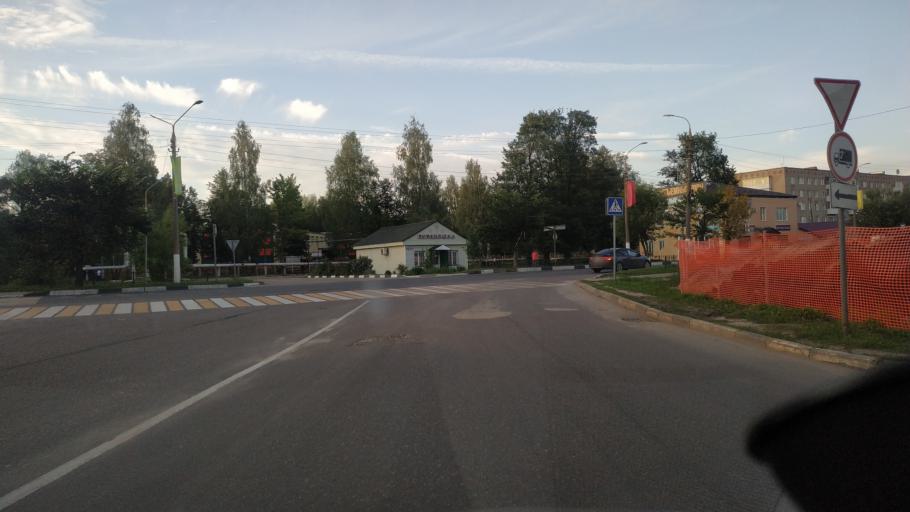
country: RU
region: Moskovskaya
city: Roshal'
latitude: 55.6631
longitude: 39.8587
